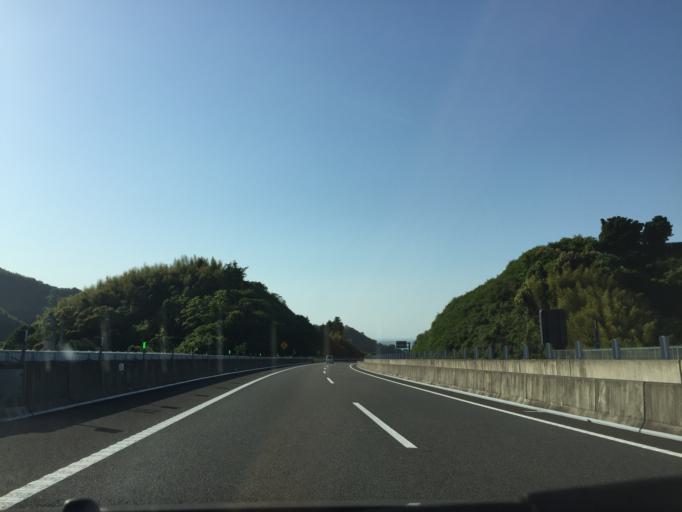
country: JP
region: Shizuoka
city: Shizuoka-shi
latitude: 35.0684
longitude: 138.4785
